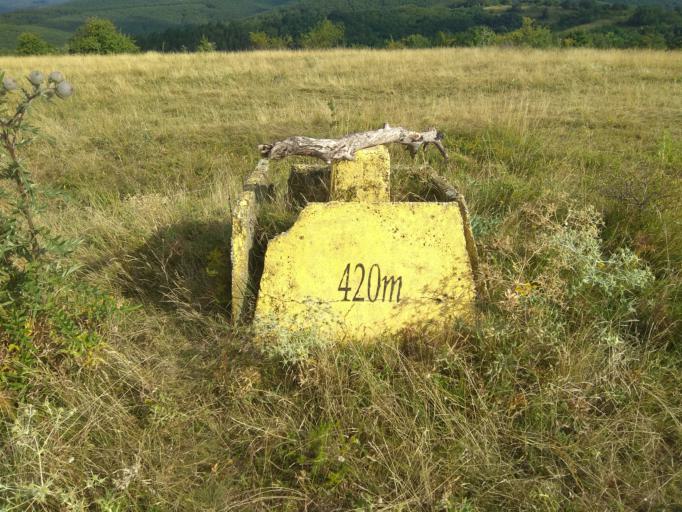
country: HU
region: Heves
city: Tarnalelesz
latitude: 48.0533
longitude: 20.2428
